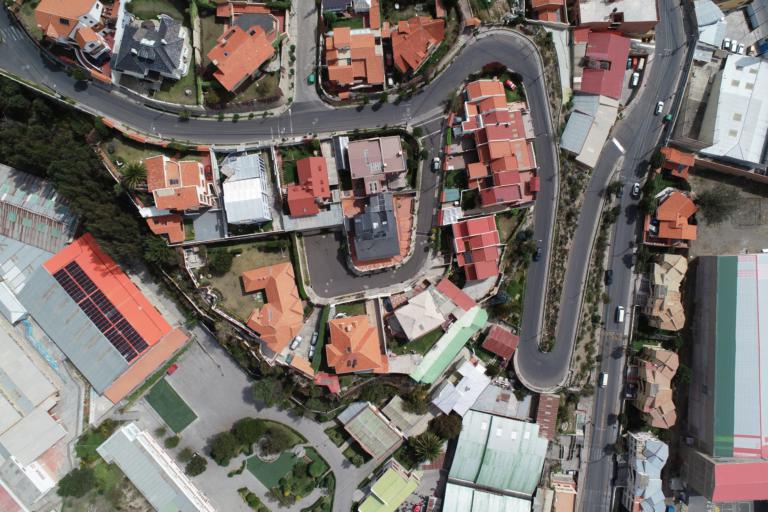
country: BO
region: La Paz
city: La Paz
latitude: -16.5360
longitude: -68.0980
